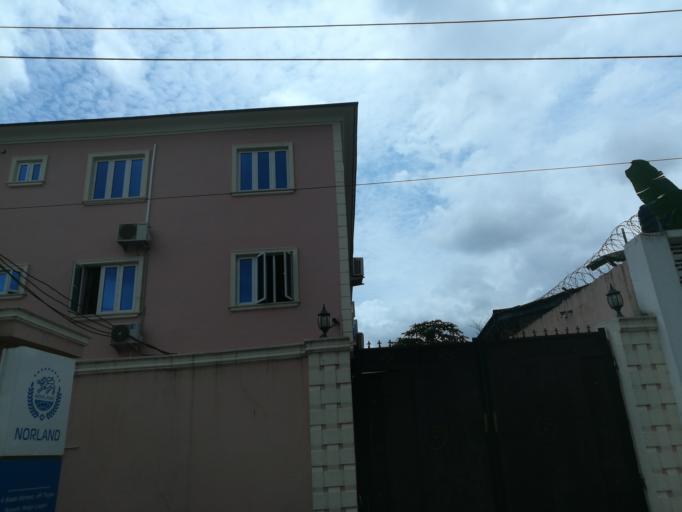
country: NG
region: Lagos
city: Ikeja
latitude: 6.5947
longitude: 3.3522
